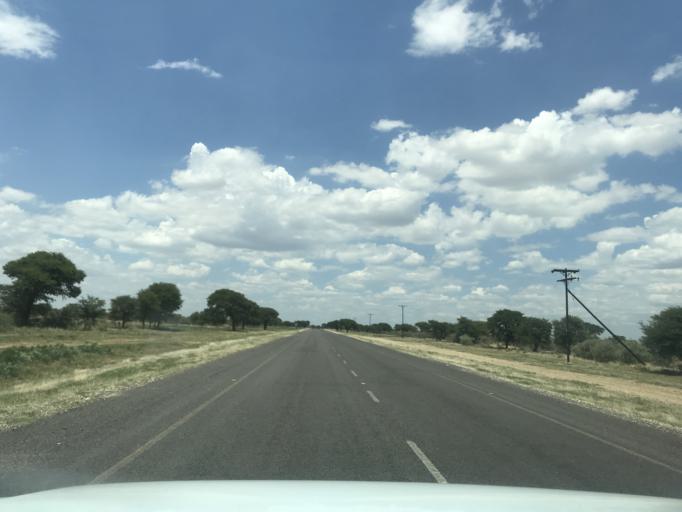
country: BW
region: South East
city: Janeng
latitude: -25.6359
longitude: 25.1529
